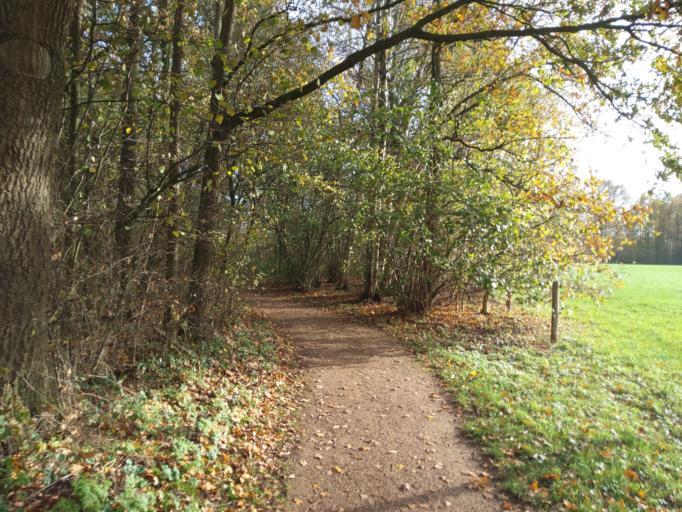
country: NL
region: Gelderland
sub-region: Gemeente Neerijnen
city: Neerijnen
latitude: 51.8346
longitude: 5.2698
